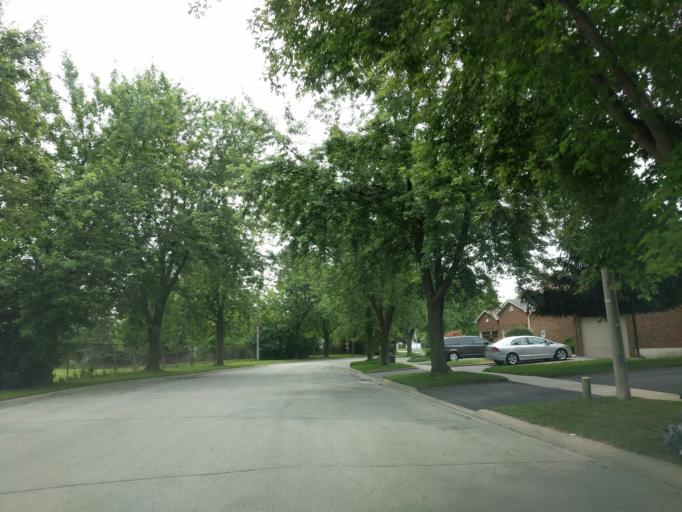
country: CA
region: Ontario
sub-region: York
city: Richmond Hill
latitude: 43.8693
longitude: -79.4194
